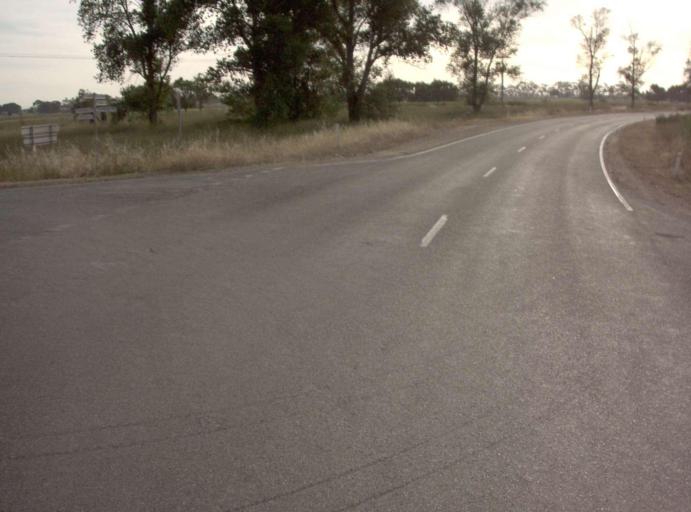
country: AU
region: Victoria
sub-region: Wellington
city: Heyfield
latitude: -37.9695
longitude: 146.9562
